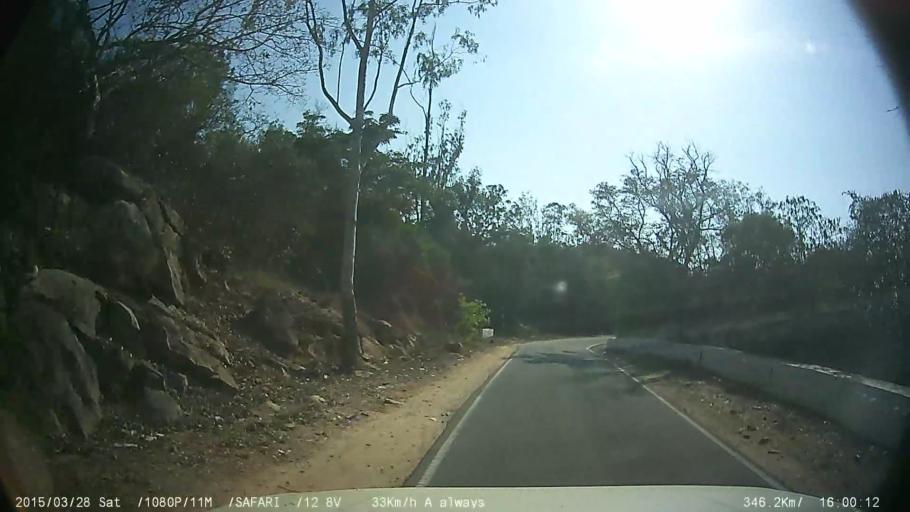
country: IN
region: Karnataka
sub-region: Mysore
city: Mysore
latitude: 12.2810
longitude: 76.6783
